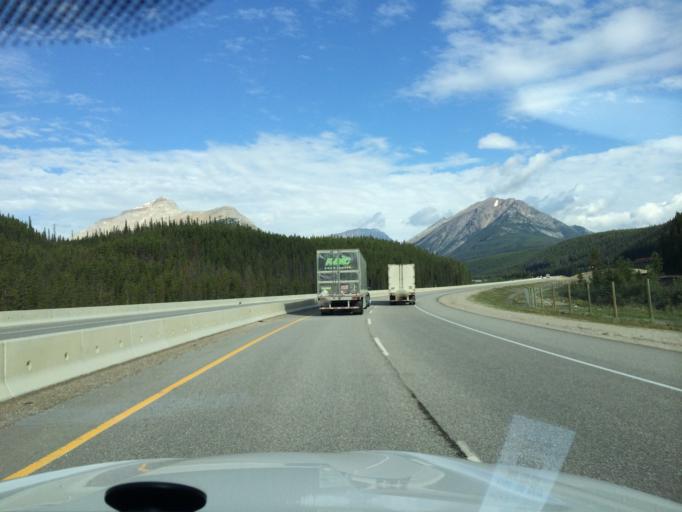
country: CA
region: Alberta
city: Lake Louise
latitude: 51.4453
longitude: -116.2492
